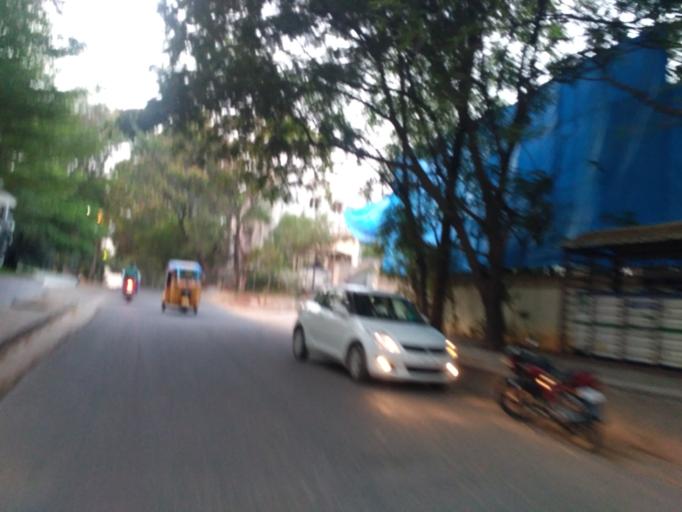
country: IN
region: Telangana
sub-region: Rangareddi
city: Kukatpalli
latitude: 17.4372
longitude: 78.4032
